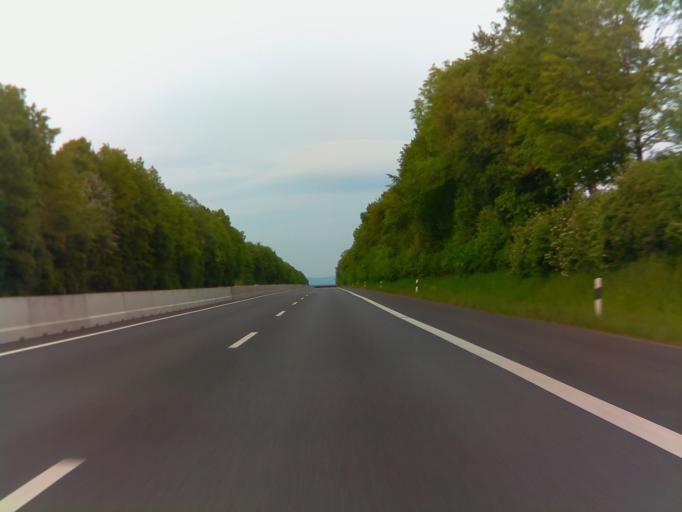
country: DE
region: Hesse
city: Borken
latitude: 51.0836
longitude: 9.2555
